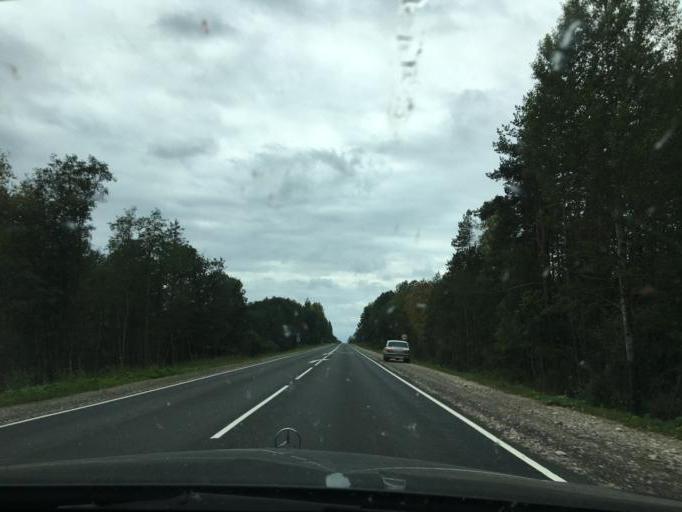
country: RU
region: Pskov
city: Pechory
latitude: 57.6677
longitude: 27.5125
